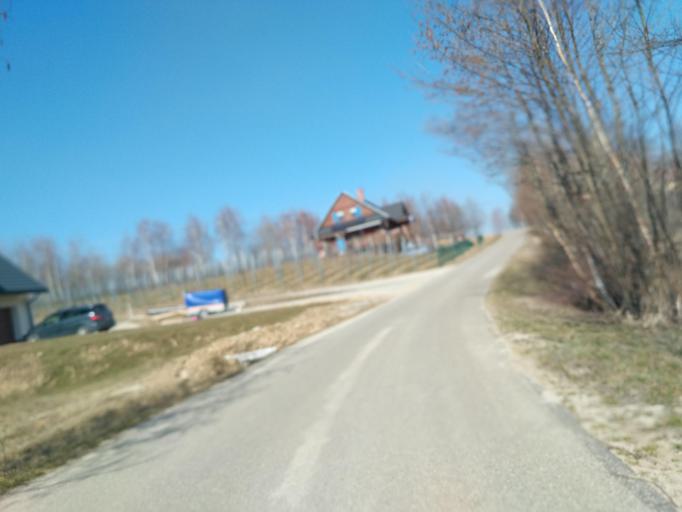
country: PL
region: Subcarpathian Voivodeship
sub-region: Powiat rzeszowski
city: Zglobien
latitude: 49.9864
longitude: 21.8450
